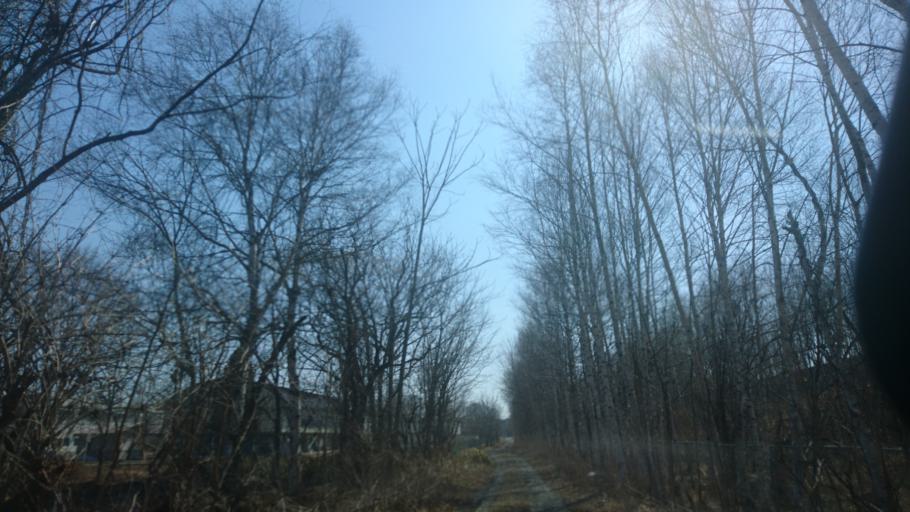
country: JP
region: Hokkaido
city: Obihiro
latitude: 42.9181
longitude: 143.1103
